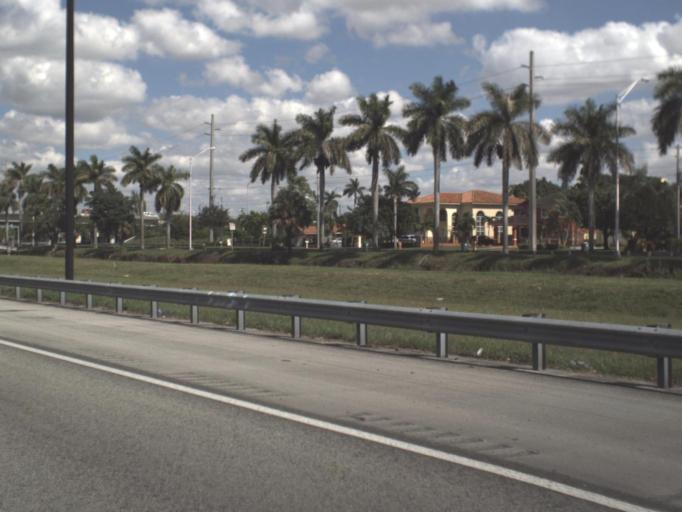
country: US
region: Florida
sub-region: Miami-Dade County
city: University Park
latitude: 25.7444
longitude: -80.3846
